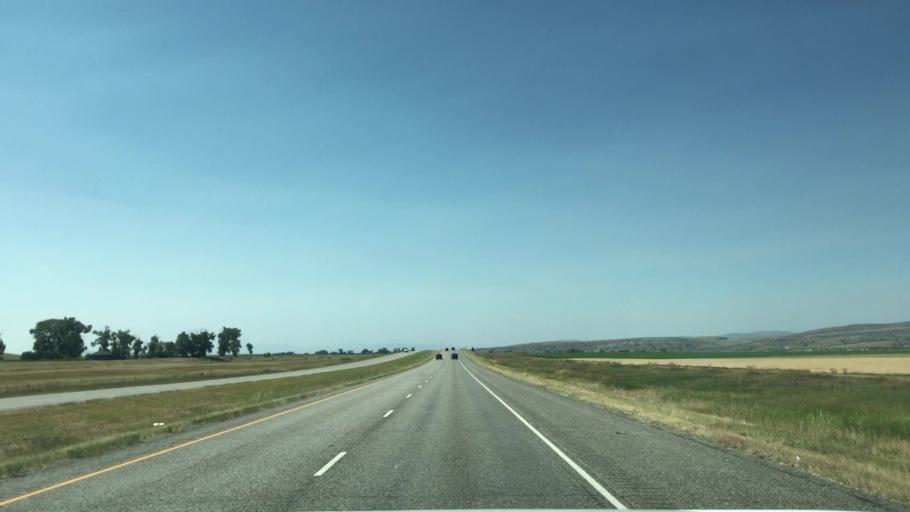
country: US
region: Montana
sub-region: Gallatin County
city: Manhattan
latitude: 45.8622
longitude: -111.3600
